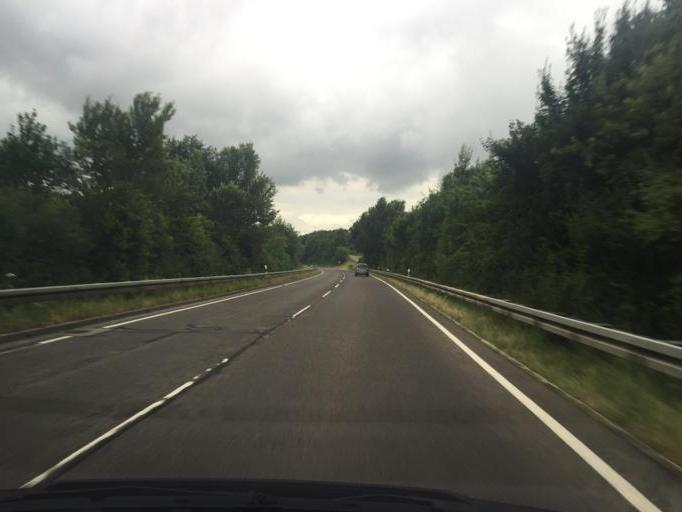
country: DE
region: Baden-Wuerttemberg
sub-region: Karlsruhe Region
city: Bretten
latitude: 49.0109
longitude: 8.7124
